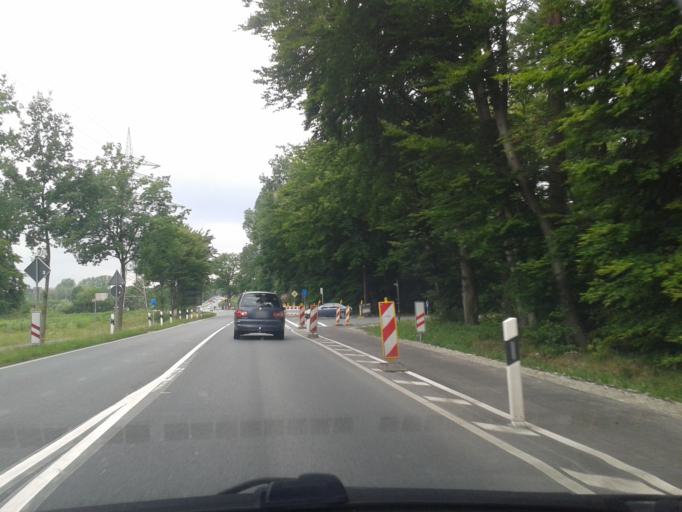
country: DE
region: North Rhine-Westphalia
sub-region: Regierungsbezirk Detmold
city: Paderborn
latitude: 51.7550
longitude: 8.7715
